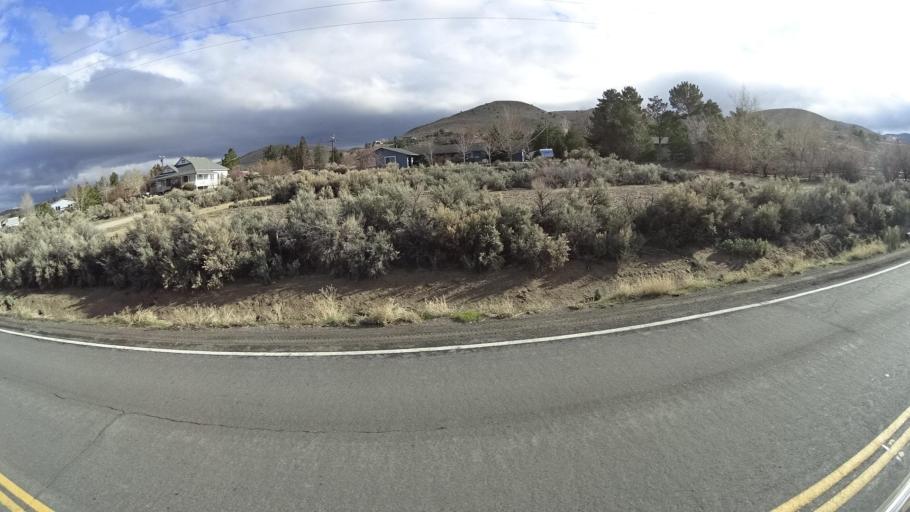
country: US
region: Nevada
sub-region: Storey County
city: Virginia City
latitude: 39.2878
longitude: -119.7625
